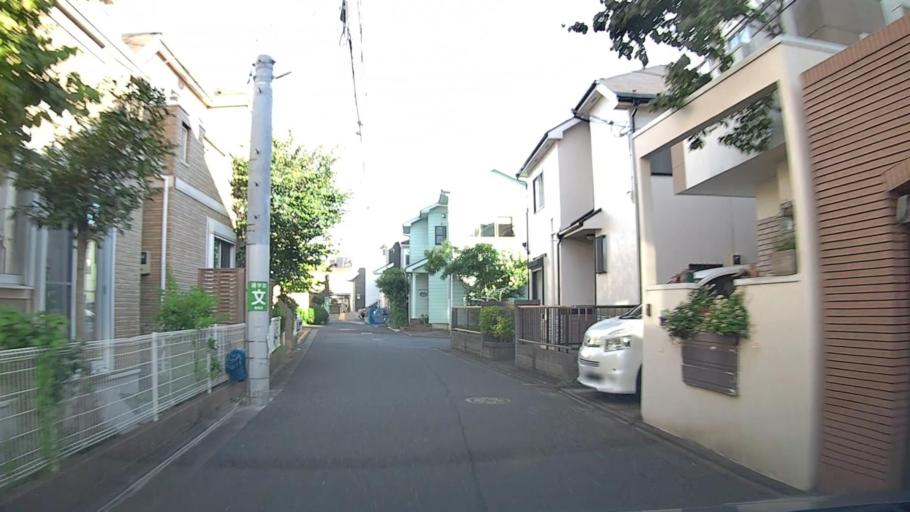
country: JP
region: Saitama
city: Wako
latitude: 35.7606
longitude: 139.6039
